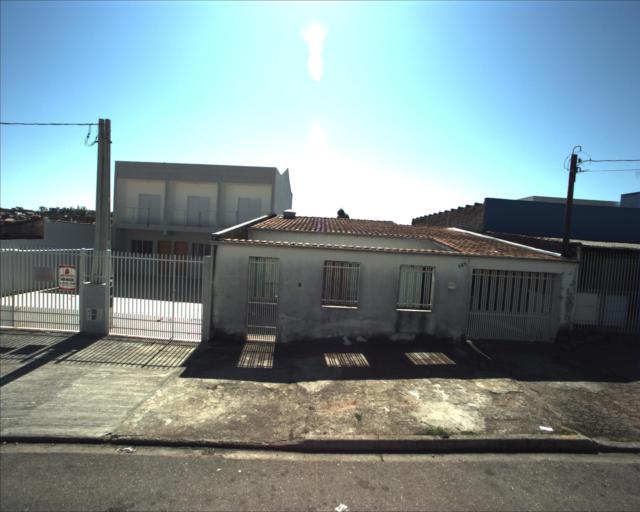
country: BR
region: Sao Paulo
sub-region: Sorocaba
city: Sorocaba
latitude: -23.4649
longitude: -47.4863
